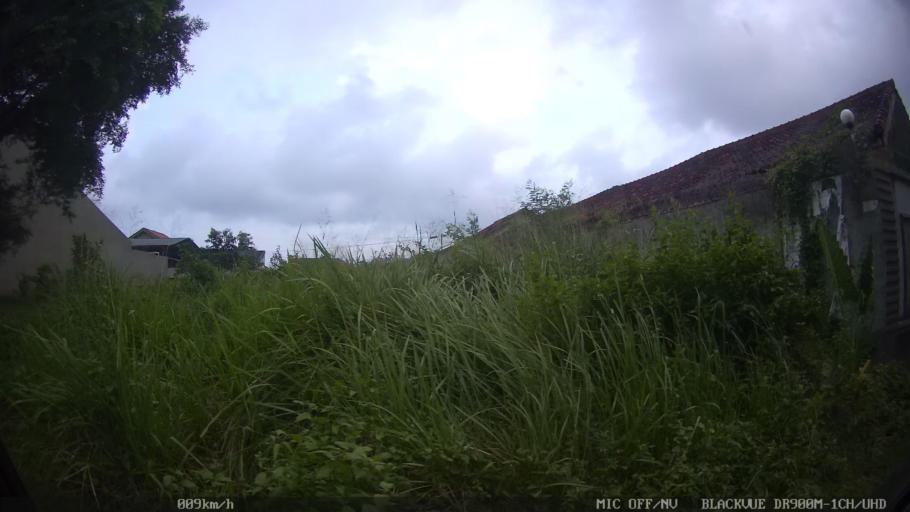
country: ID
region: Lampung
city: Bandarlampung
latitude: -5.4090
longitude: 105.2748
